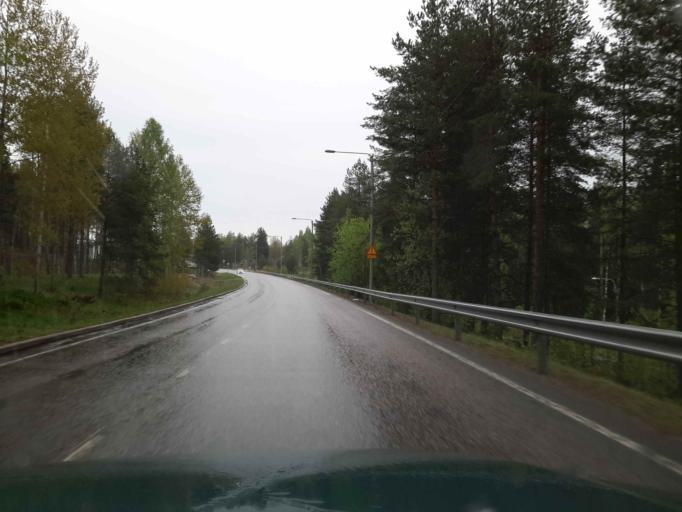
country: FI
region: Uusimaa
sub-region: Helsinki
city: Vihti
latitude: 60.3244
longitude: 24.2782
